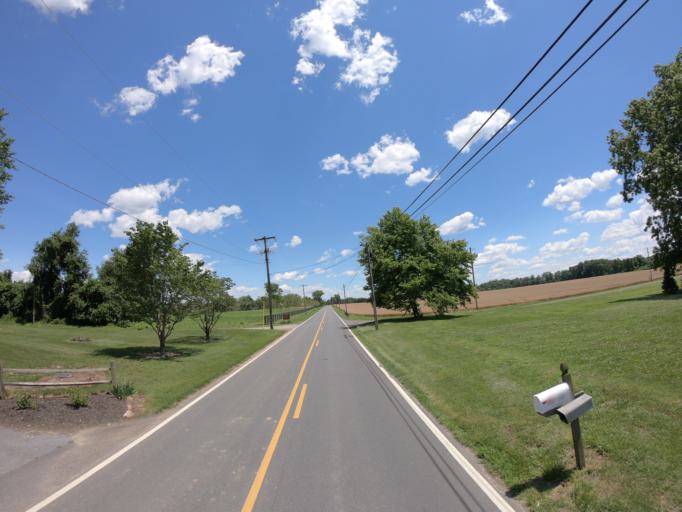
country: US
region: Delaware
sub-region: New Castle County
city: Middletown
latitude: 39.4625
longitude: -75.7580
